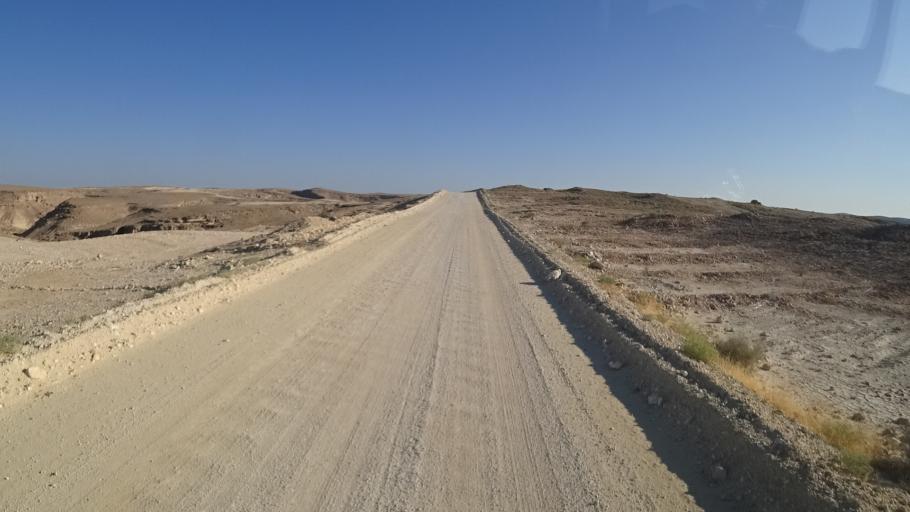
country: YE
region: Al Mahrah
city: Hawf
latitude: 17.2360
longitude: 53.3194
